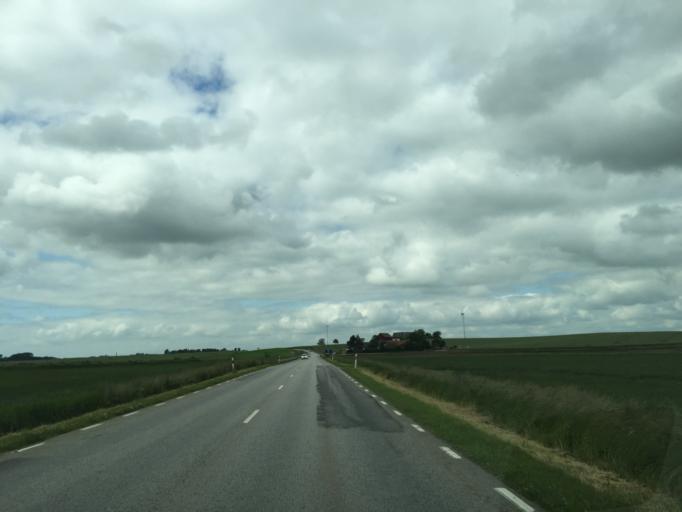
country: SE
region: Skane
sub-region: Svedala Kommun
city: Klagerup
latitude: 55.6154
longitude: 13.2625
